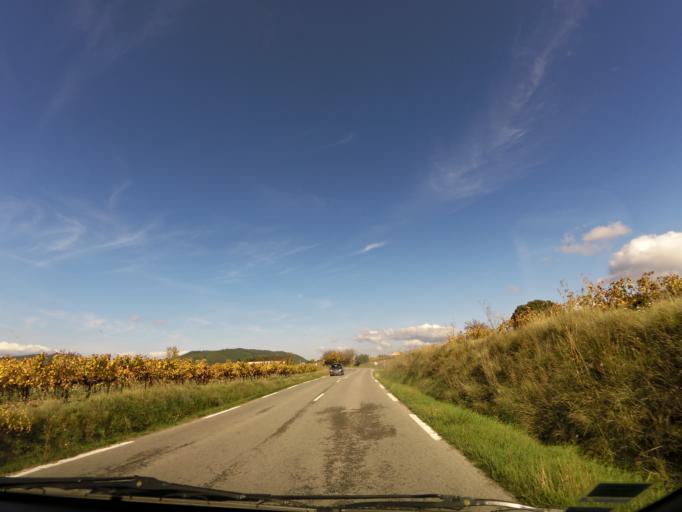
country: FR
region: Languedoc-Roussillon
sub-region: Departement du Gard
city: Saint-Mamert-du-Gard
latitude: 43.8870
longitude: 4.0985
